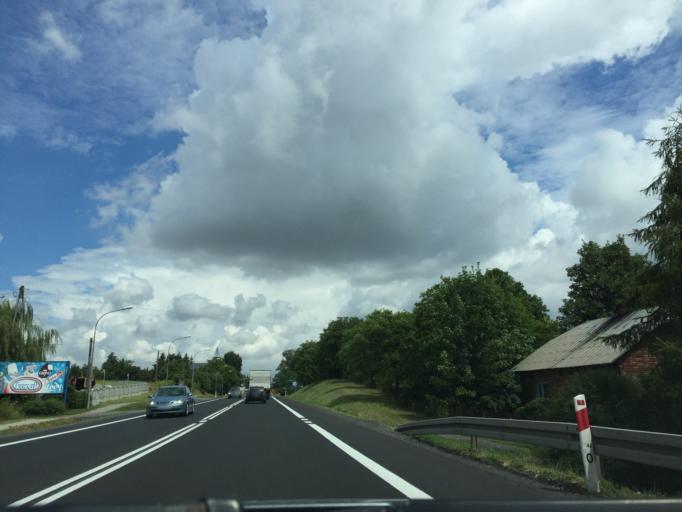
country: PL
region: Lesser Poland Voivodeship
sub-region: Powiat krakowski
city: Michalowice
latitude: 50.1994
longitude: 20.0097
